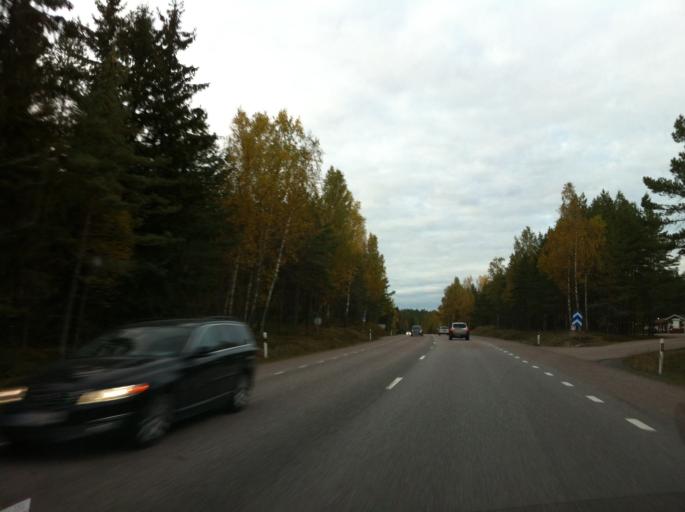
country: SE
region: OErebro
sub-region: Orebro Kommun
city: Hovsta
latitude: 59.4377
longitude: 15.1545
